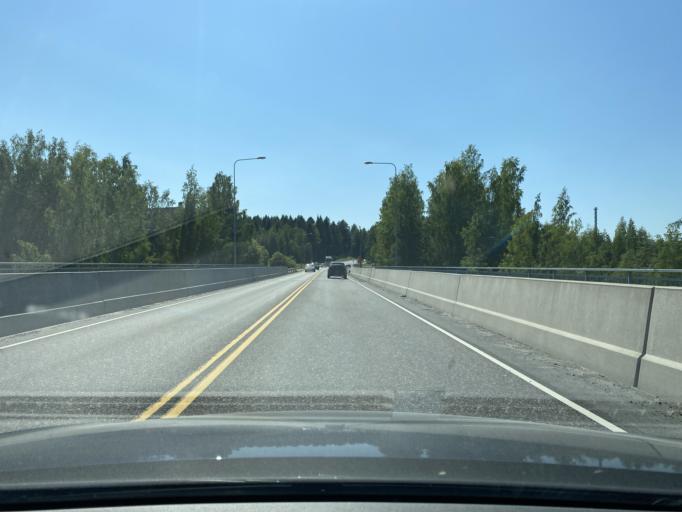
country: FI
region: Pirkanmaa
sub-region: Tampere
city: Nokia
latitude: 61.4701
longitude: 23.5252
